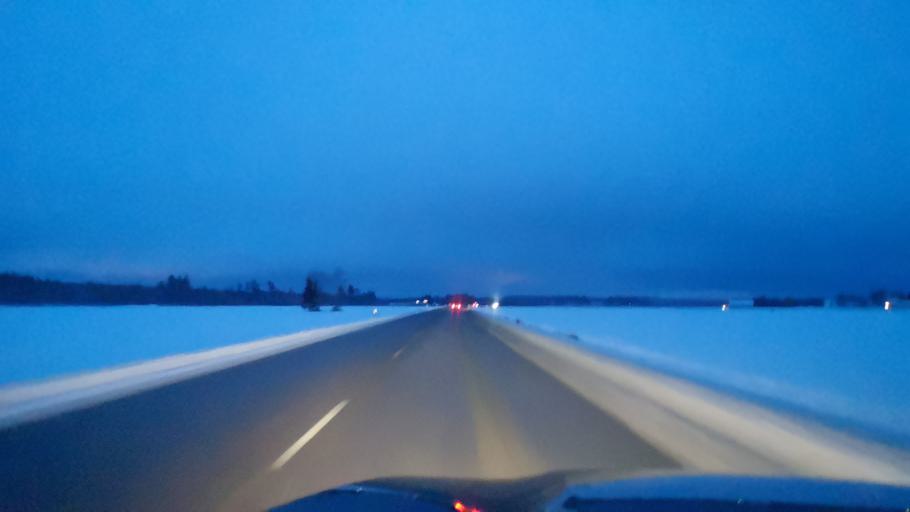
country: FI
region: Varsinais-Suomi
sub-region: Loimaa
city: Loimaa
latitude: 60.8881
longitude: 23.0972
